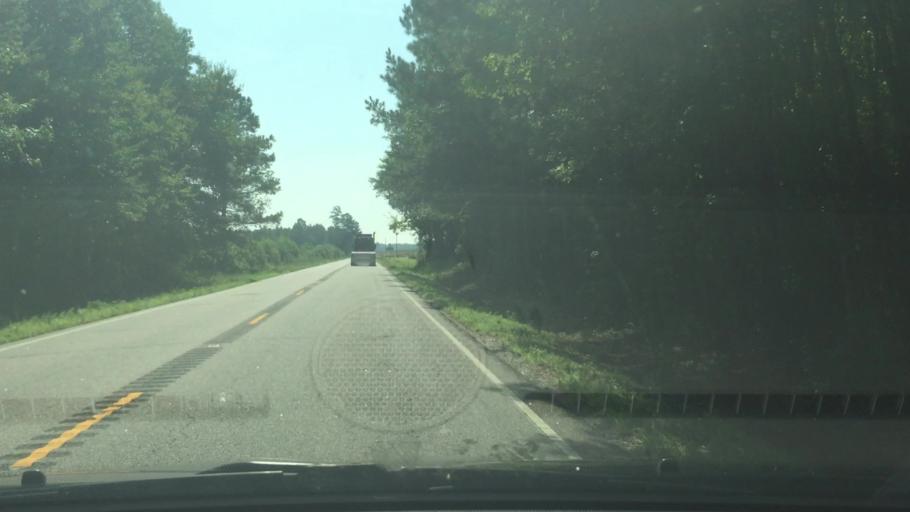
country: US
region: Virginia
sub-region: Sussex County
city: Sussex
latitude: 36.9830
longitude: -77.2416
